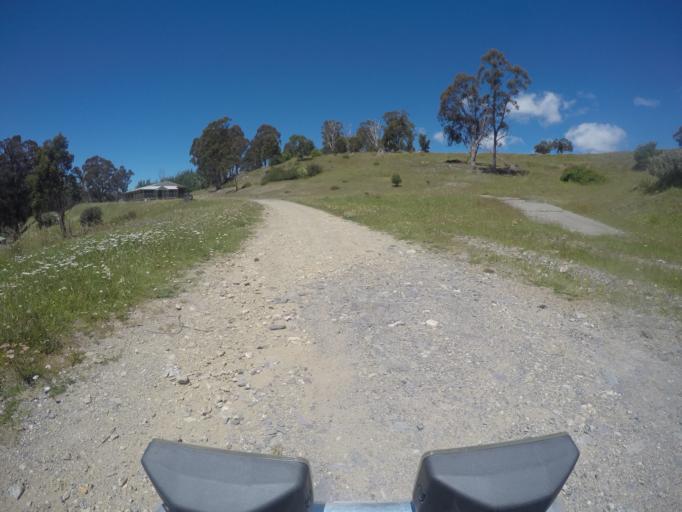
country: AU
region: New South Wales
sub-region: Snowy River
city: Jindabyne
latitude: -35.9372
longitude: 148.3800
